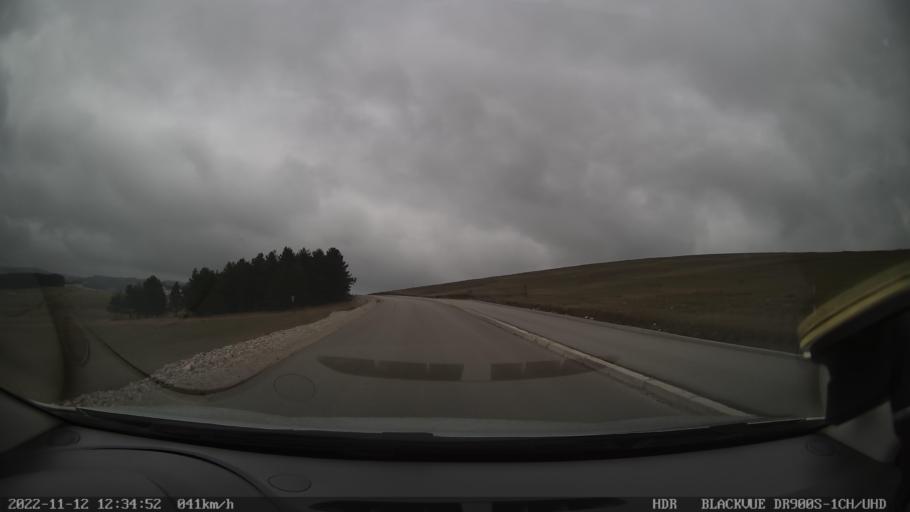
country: RS
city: Zlatibor
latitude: 43.7144
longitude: 19.7158
